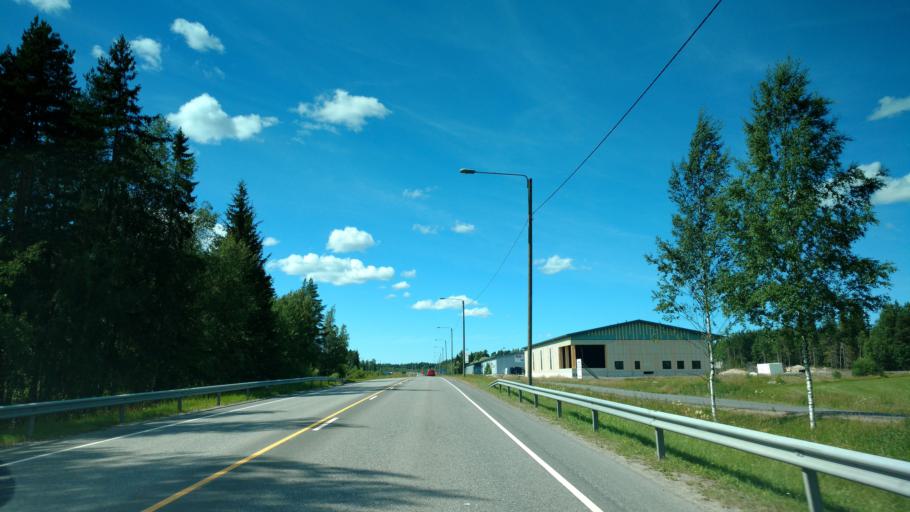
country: FI
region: Varsinais-Suomi
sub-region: Turku
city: Lieto
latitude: 60.4598
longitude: 22.4312
